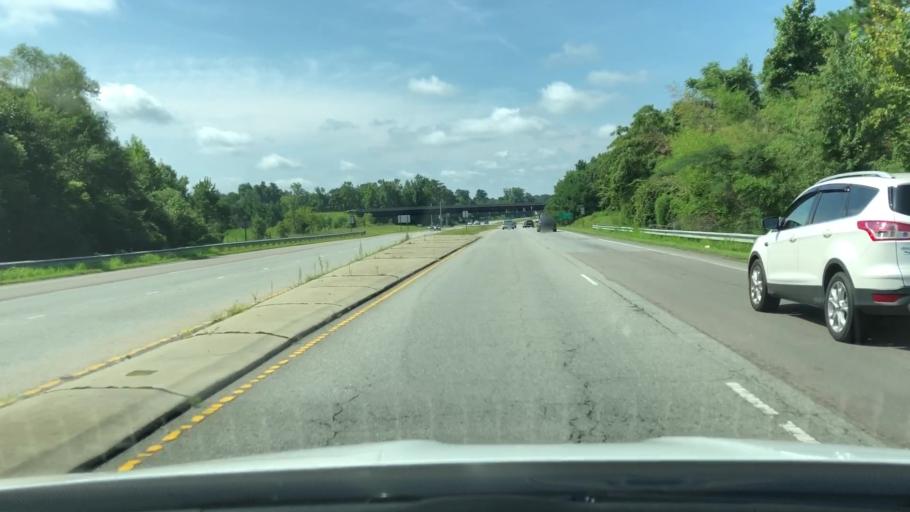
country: US
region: North Carolina
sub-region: Martin County
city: Williamston
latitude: 35.8442
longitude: -77.0518
